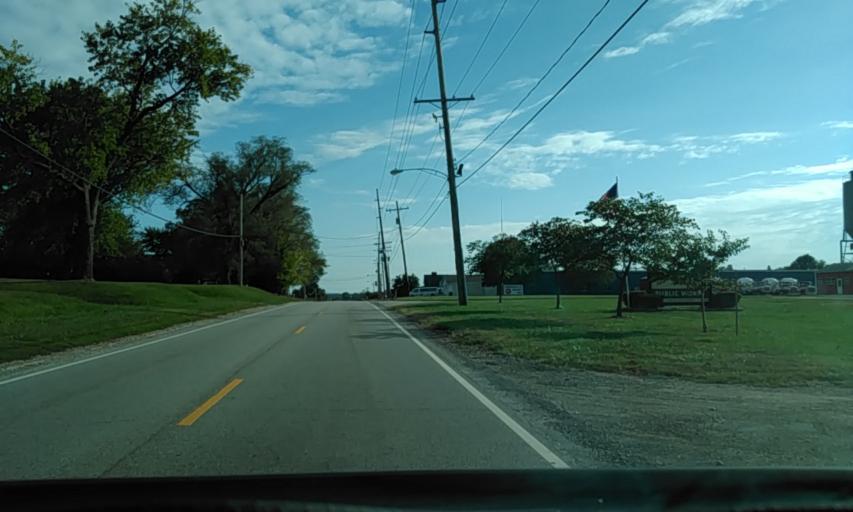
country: US
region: Illinois
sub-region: Bond County
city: Greenville
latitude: 38.8815
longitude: -89.4144
